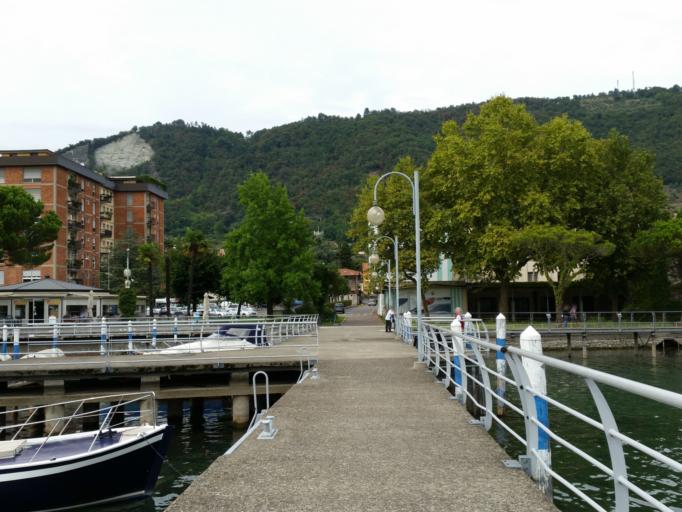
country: IT
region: Lombardy
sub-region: Provincia di Bergamo
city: Sarnico
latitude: 45.6666
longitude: 9.9641
